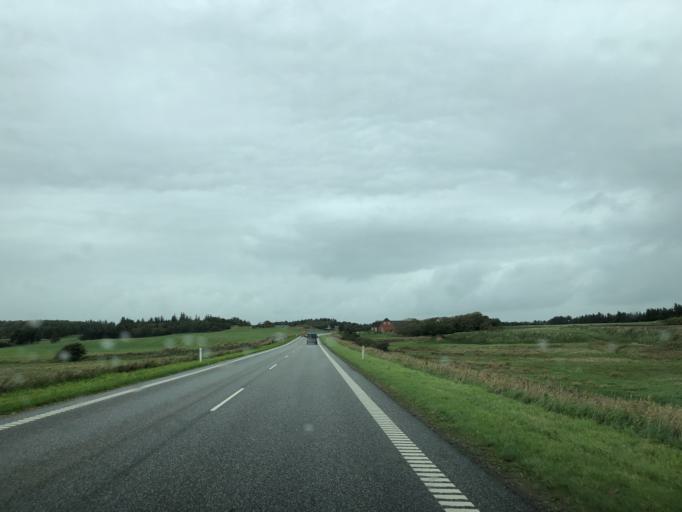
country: DK
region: Central Jutland
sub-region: Struer Kommune
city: Struer
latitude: 56.5953
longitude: 8.5255
